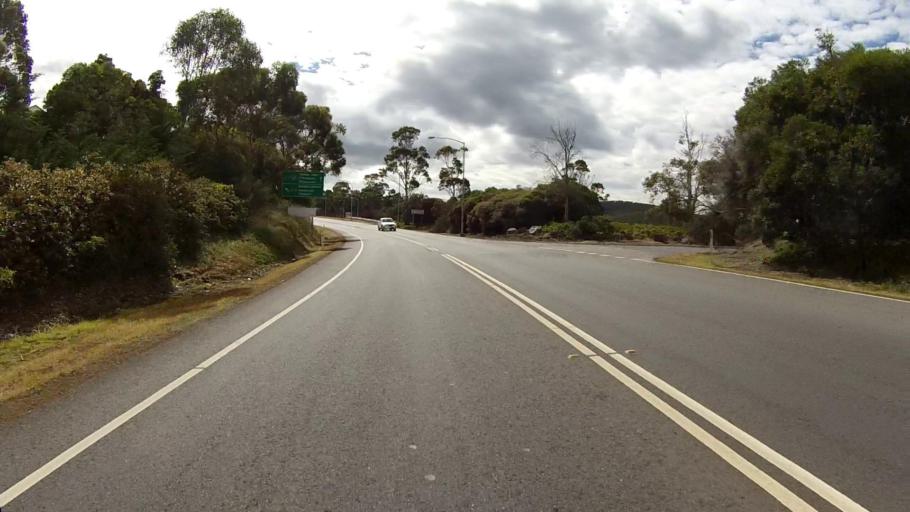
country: AU
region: Tasmania
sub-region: Glenorchy
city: Lutana
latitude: -42.8147
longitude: 147.3125
